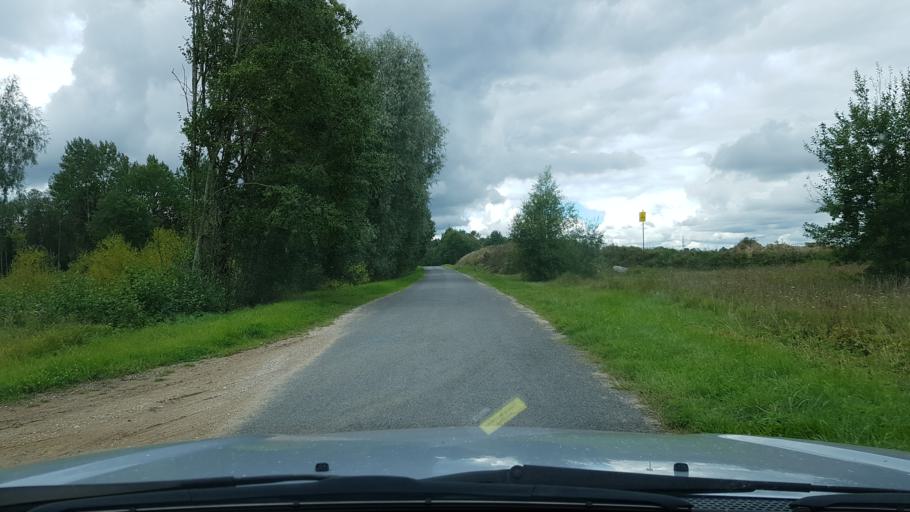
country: EE
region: Harju
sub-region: Rae vald
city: Vaida
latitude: 59.3009
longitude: 25.0099
